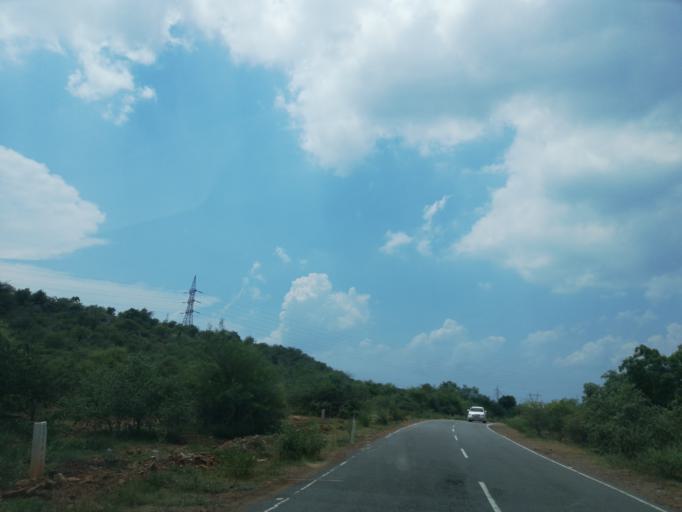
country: IN
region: Andhra Pradesh
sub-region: Guntur
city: Macherla
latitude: 16.5622
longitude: 79.3517
